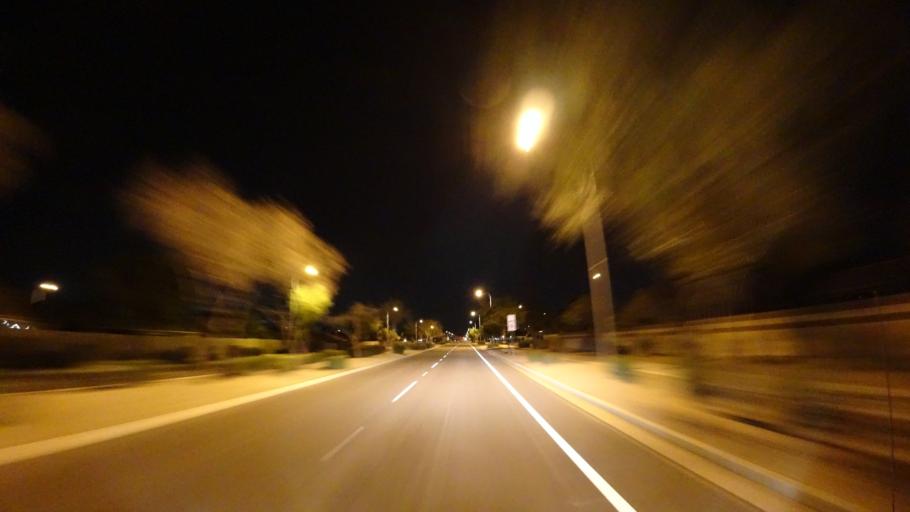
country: US
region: Arizona
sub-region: Maricopa County
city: Sun Lakes
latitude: 33.2059
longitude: -111.8063
